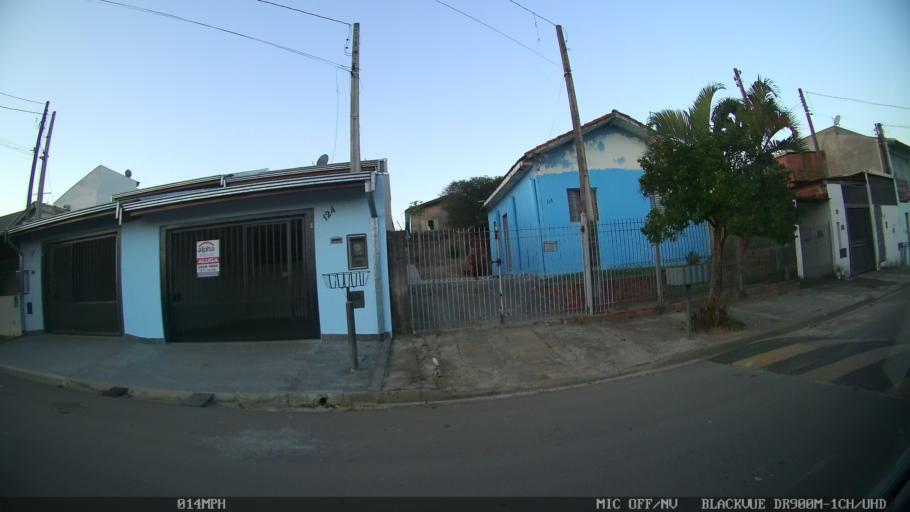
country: BR
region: Sao Paulo
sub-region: Sumare
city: Sumare
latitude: -22.8144
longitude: -47.2286
